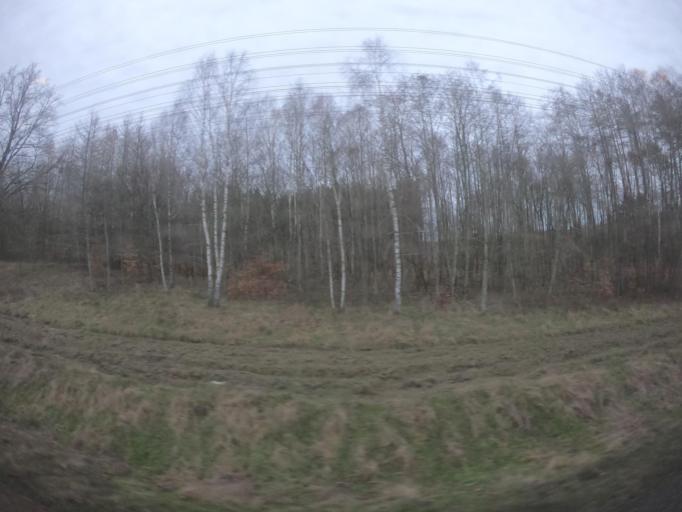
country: PL
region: West Pomeranian Voivodeship
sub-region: Powiat szczecinecki
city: Borne Sulinowo
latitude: 53.6590
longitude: 16.5621
